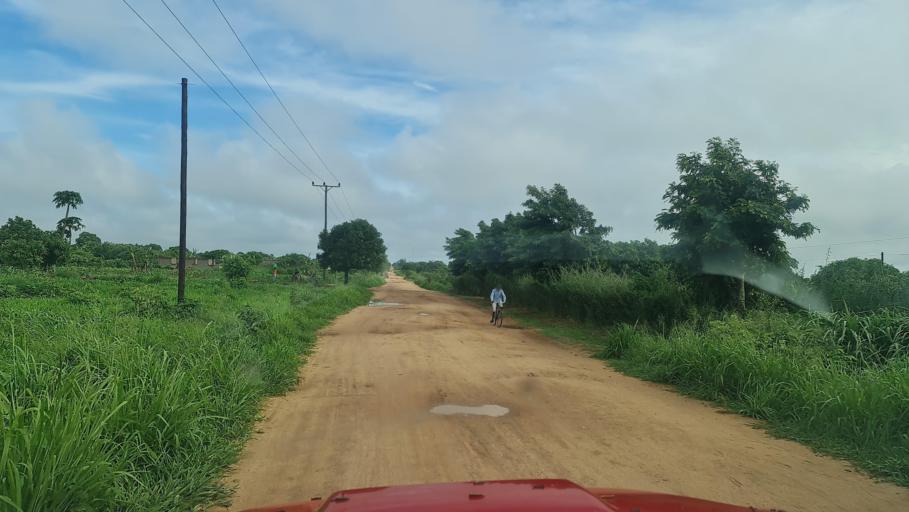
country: MW
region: Southern Region
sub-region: Nsanje District
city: Nsanje
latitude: -17.3152
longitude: 35.5923
